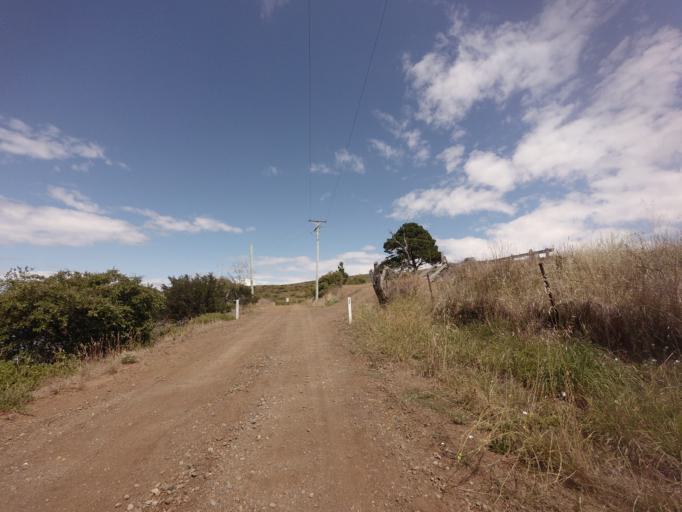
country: AU
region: Tasmania
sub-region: Clarence
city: Rokeby
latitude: -42.9180
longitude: 147.4342
